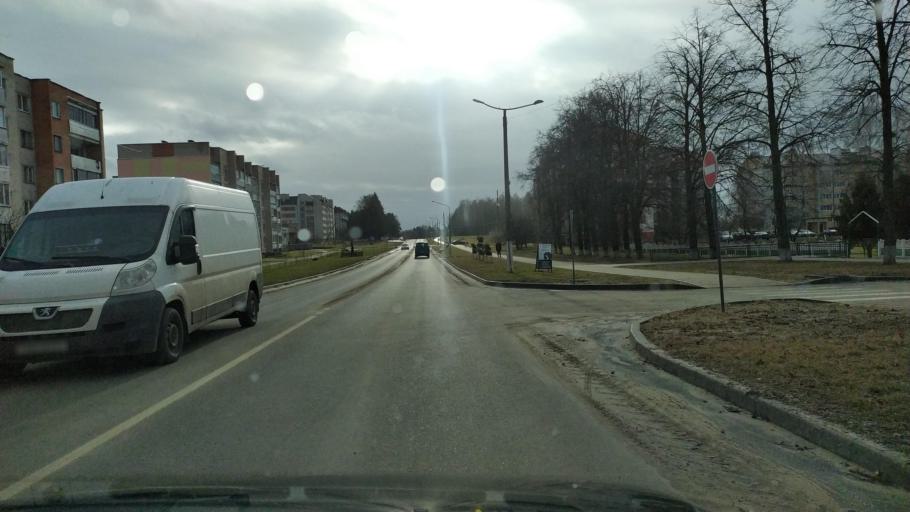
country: BY
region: Brest
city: Kamyanyets
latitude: 52.3940
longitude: 23.8234
